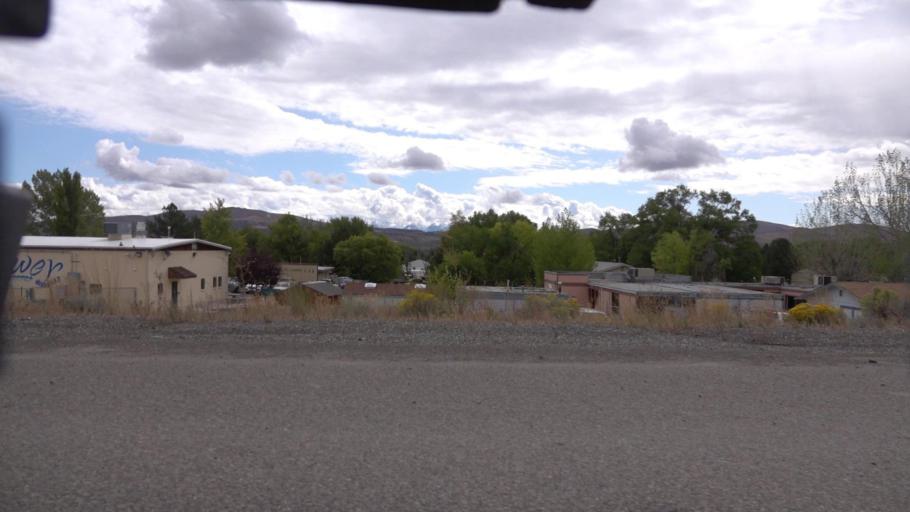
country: US
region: Nevada
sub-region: Elko County
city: Elko
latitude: 40.8414
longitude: -115.7748
